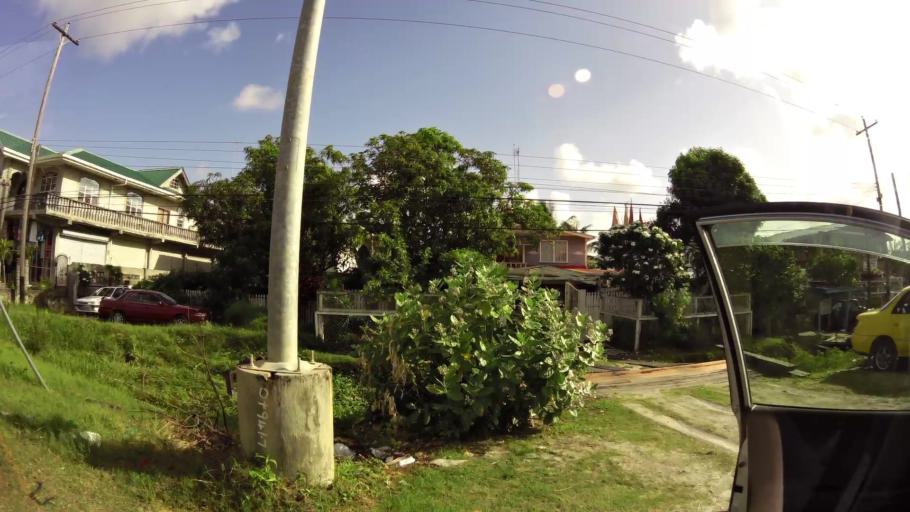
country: GY
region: Demerara-Mahaica
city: Georgetown
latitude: 6.8175
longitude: -58.0815
